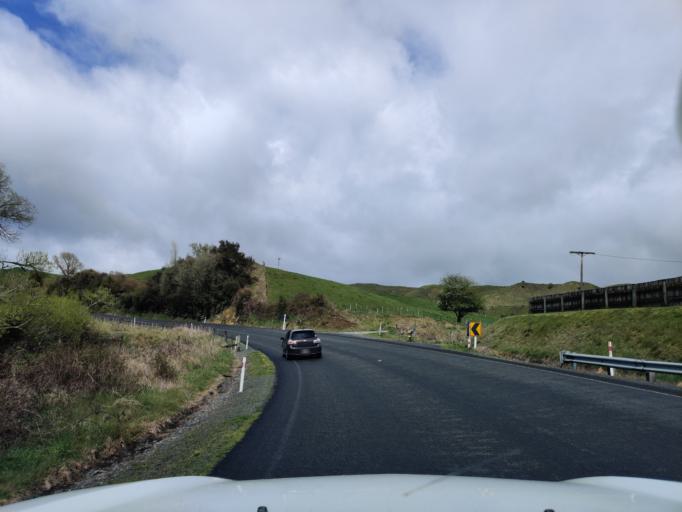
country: NZ
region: Waikato
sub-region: Otorohanga District
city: Otorohanga
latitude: -38.6018
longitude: 175.2155
